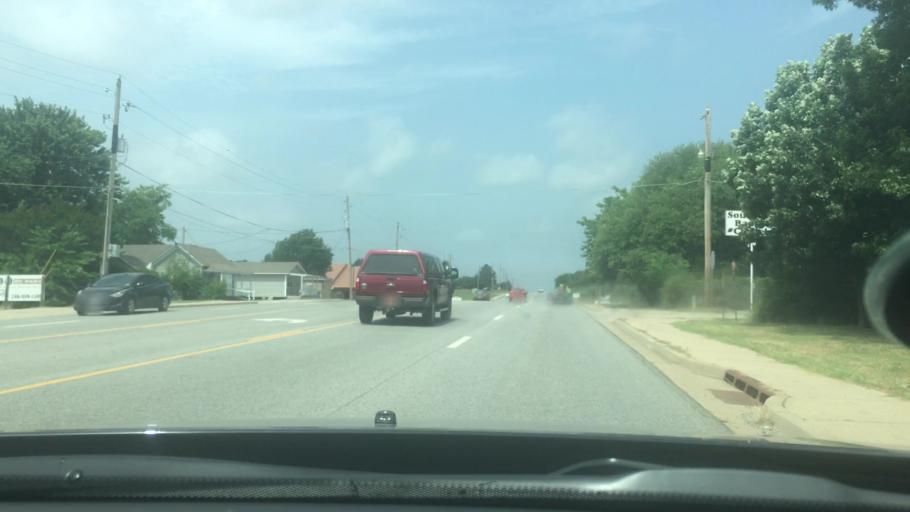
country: US
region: Oklahoma
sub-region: Atoka County
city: Atoka
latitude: 34.3749
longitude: -96.1394
